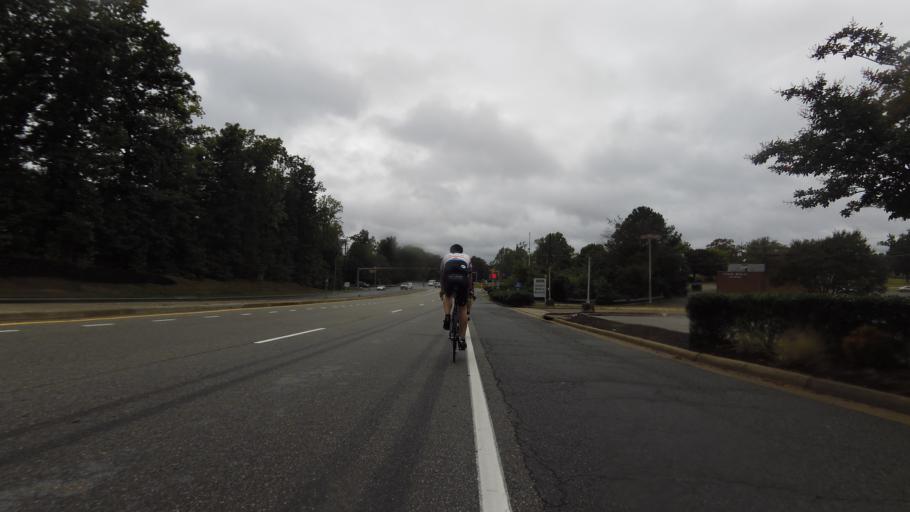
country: US
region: Virginia
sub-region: Henrico County
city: Tuckahoe
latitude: 37.5962
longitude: -77.5926
